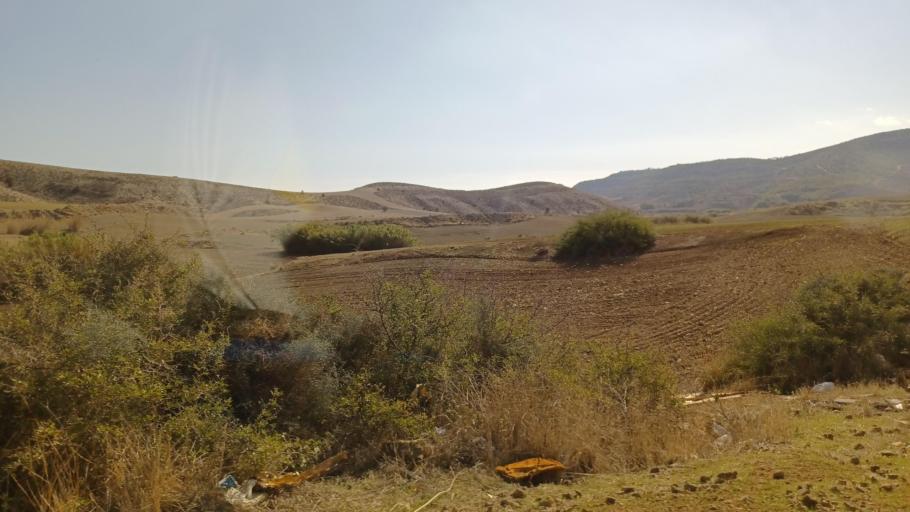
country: CY
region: Larnaka
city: Voroklini
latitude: 35.0155
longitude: 33.6448
